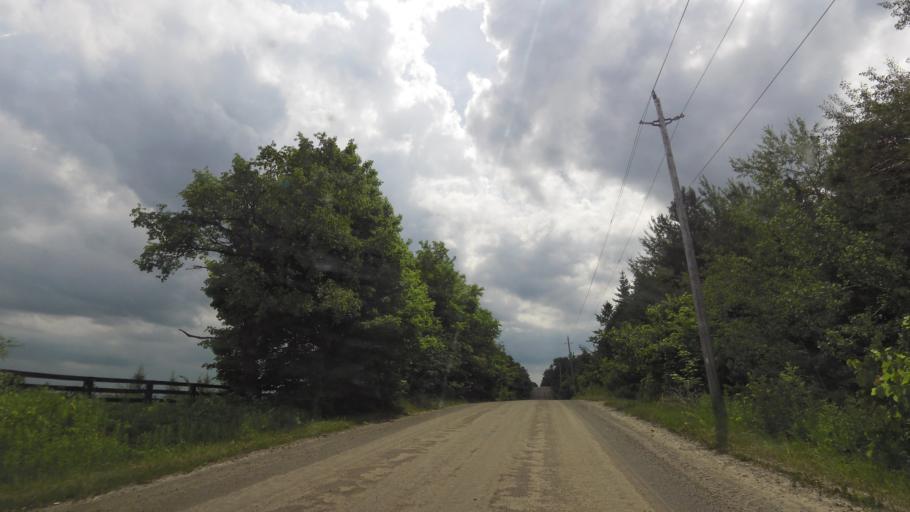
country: CA
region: Ontario
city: Orangeville
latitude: 43.8720
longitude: -79.9340
